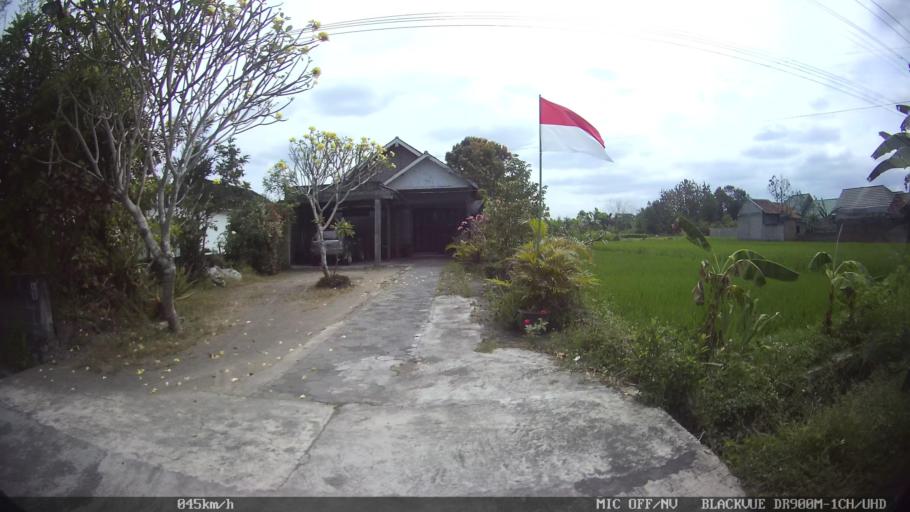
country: ID
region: Central Java
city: Candi Prambanan
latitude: -7.7468
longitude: 110.4811
